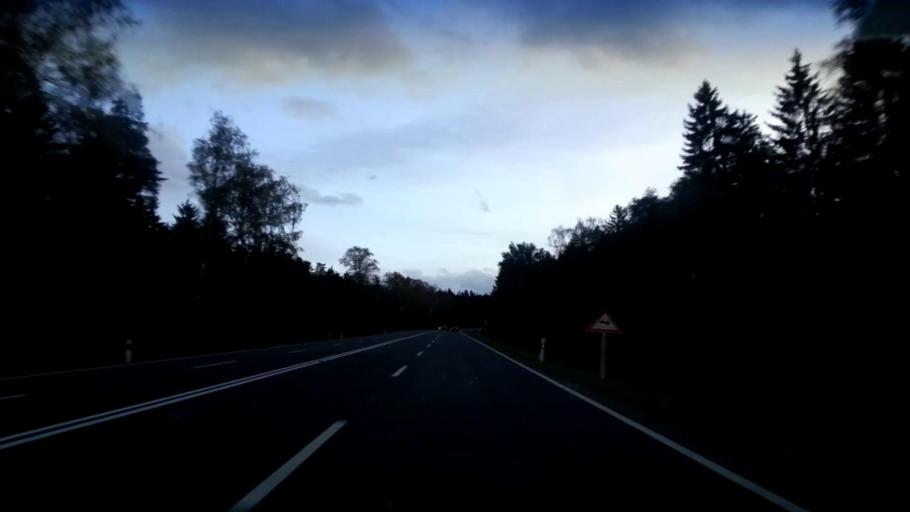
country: DE
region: Bavaria
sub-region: Upper Franconia
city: Trostau
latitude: 50.0107
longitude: 11.9258
